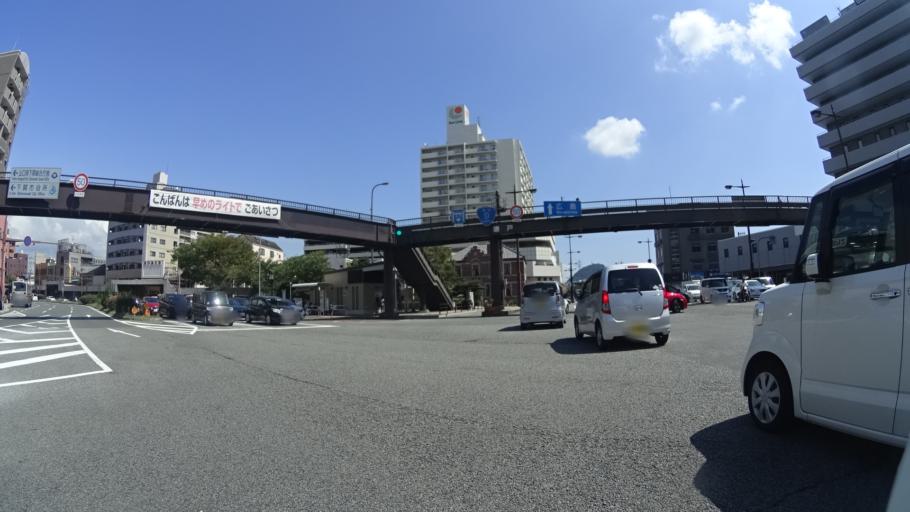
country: JP
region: Yamaguchi
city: Shimonoseki
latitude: 33.9567
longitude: 130.9423
